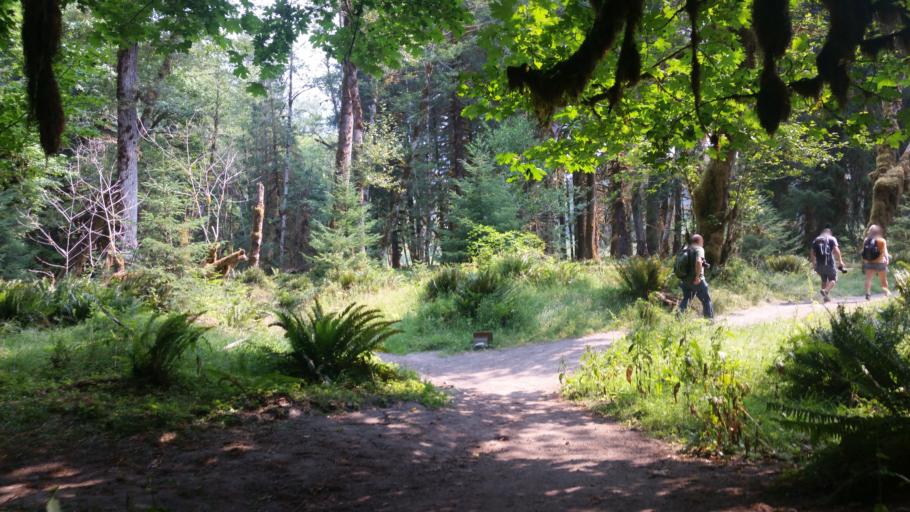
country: US
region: Washington
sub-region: Clallam County
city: Forks
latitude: 47.8600
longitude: -123.9264
